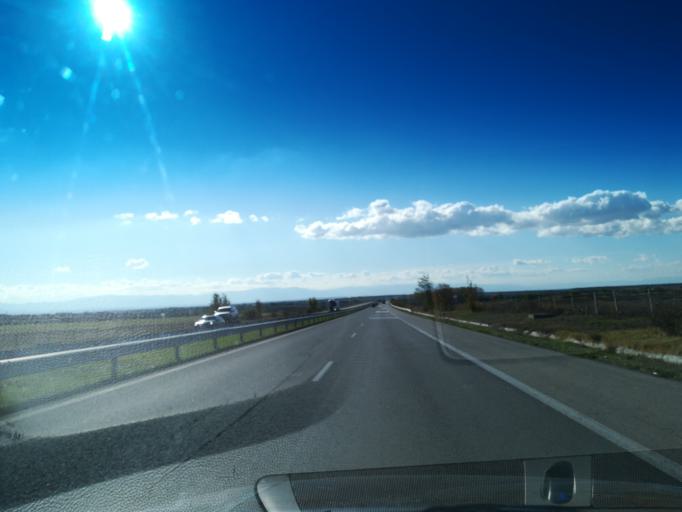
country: BG
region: Stara Zagora
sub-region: Obshtina Chirpan
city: Chirpan
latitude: 42.2222
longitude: 25.3373
